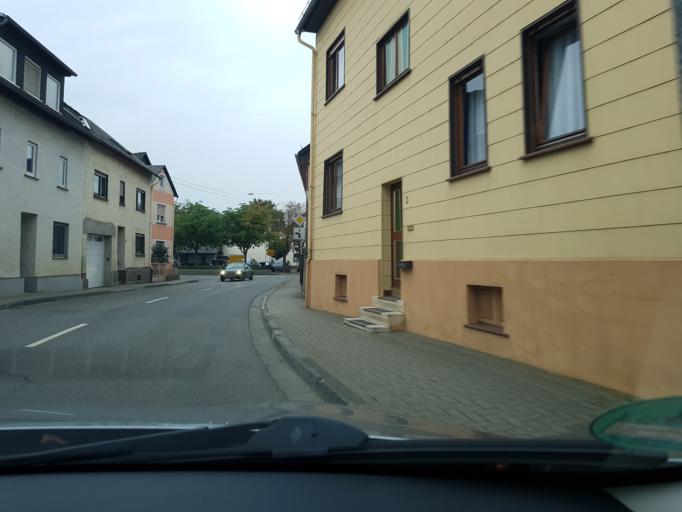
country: DE
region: Rheinland-Pfalz
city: Miehlen
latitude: 50.2289
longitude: 7.8285
